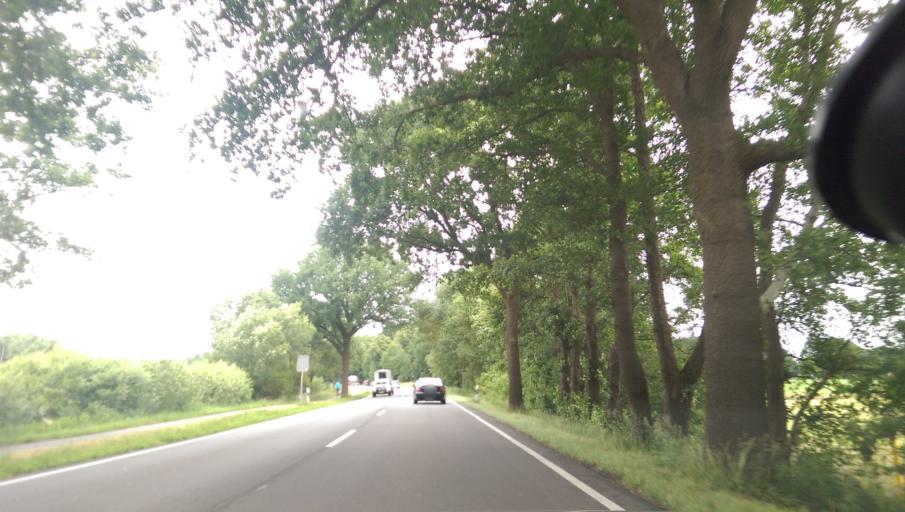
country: DE
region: Lower Saxony
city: Botersen
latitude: 53.1587
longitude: 9.3225
